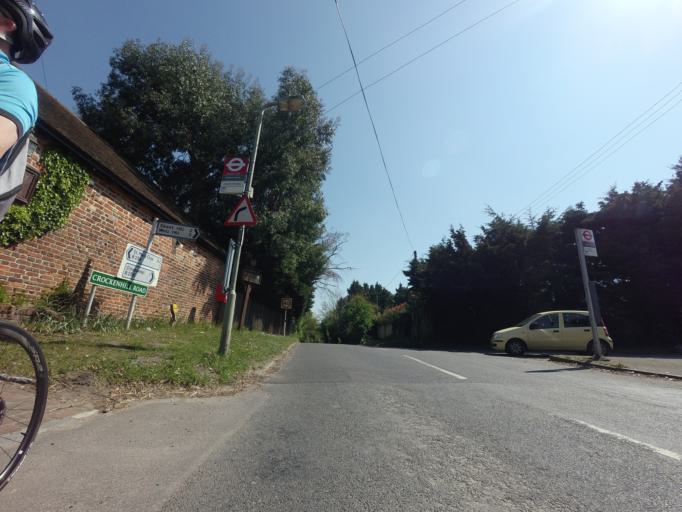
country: GB
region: England
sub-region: Greater London
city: Orpington
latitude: 51.3869
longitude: 0.1316
